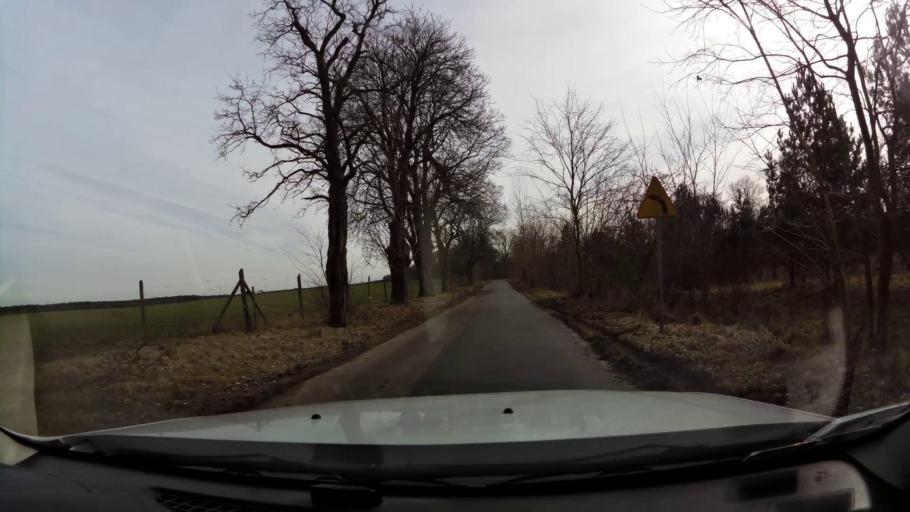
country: PL
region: West Pomeranian Voivodeship
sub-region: Powiat stargardzki
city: Insko
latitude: 53.4546
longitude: 15.6195
